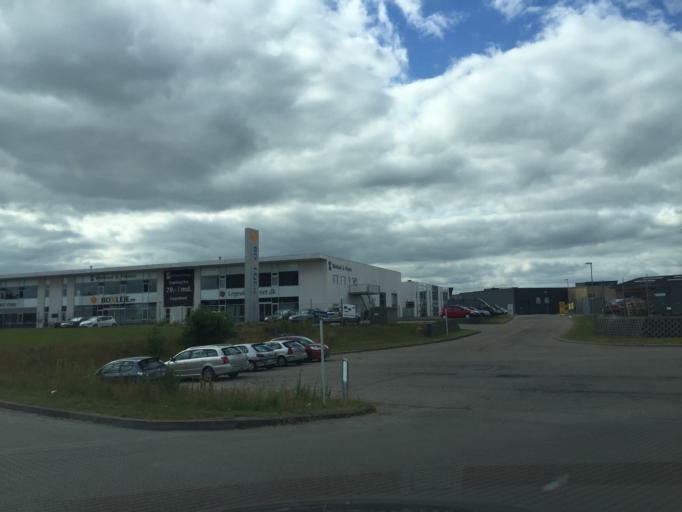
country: DK
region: South Denmark
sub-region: Fredericia Kommune
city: Snoghoj
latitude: 55.5311
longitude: 9.7148
